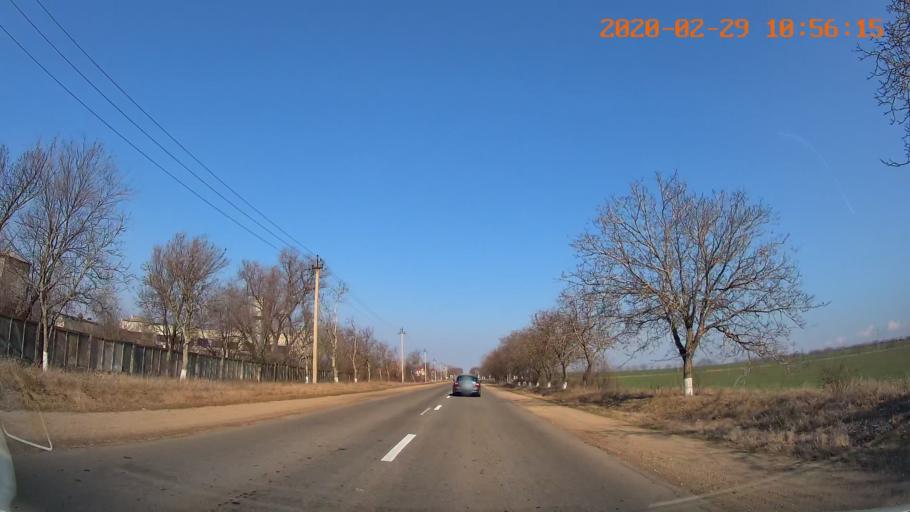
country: MD
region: Telenesti
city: Grigoriopol
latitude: 47.1435
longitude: 29.3251
